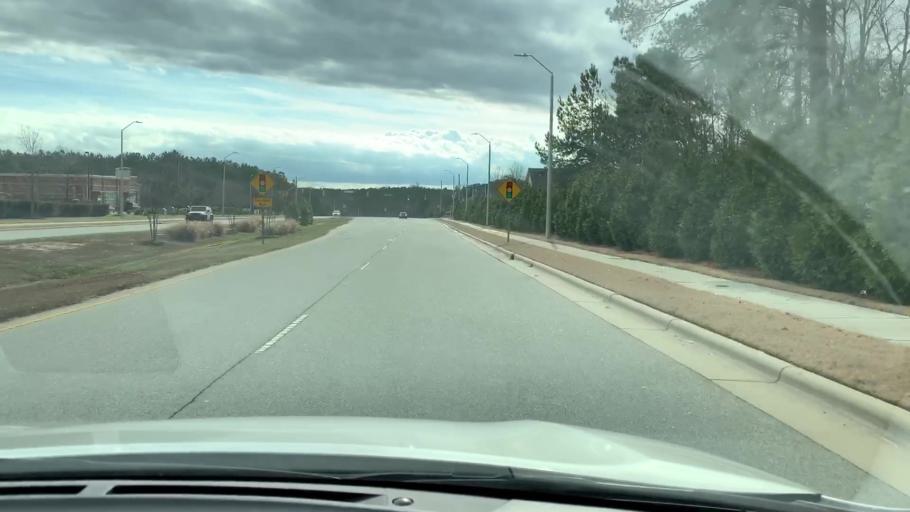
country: US
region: North Carolina
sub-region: Wake County
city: Green Level
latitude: 35.8205
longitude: -78.9026
